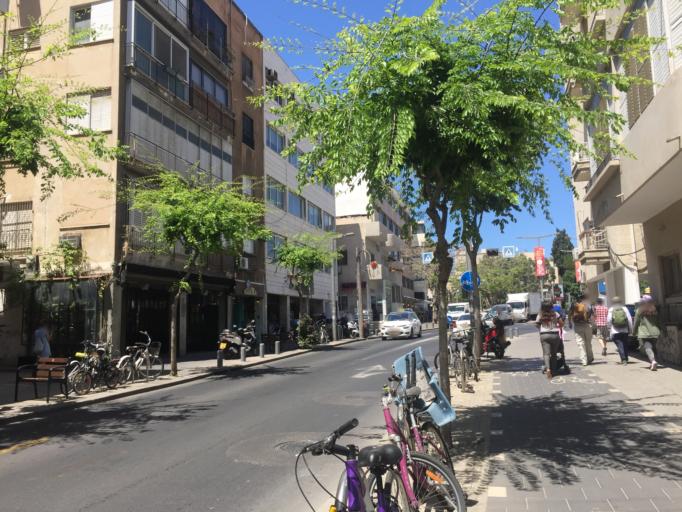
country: IL
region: Tel Aviv
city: Tel Aviv
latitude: 32.0716
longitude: 34.7805
